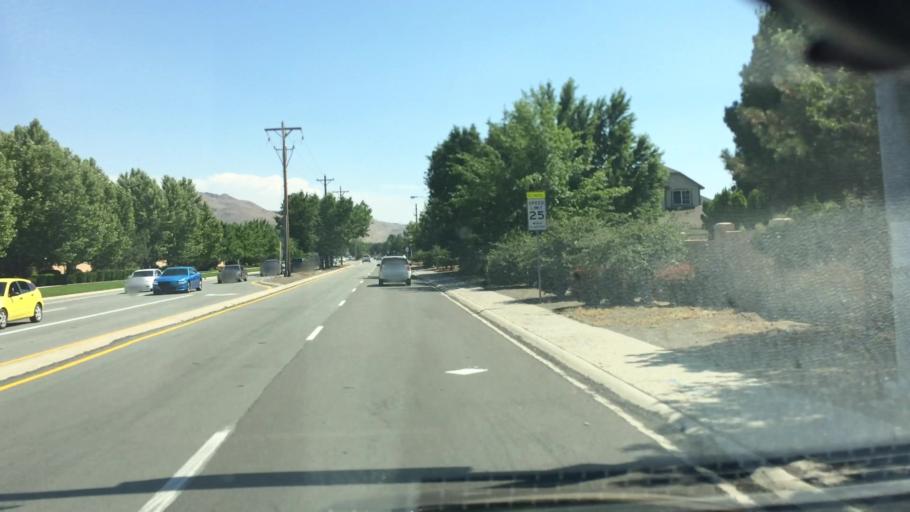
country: US
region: Nevada
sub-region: Washoe County
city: Sparks
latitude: 39.5508
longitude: -119.7058
